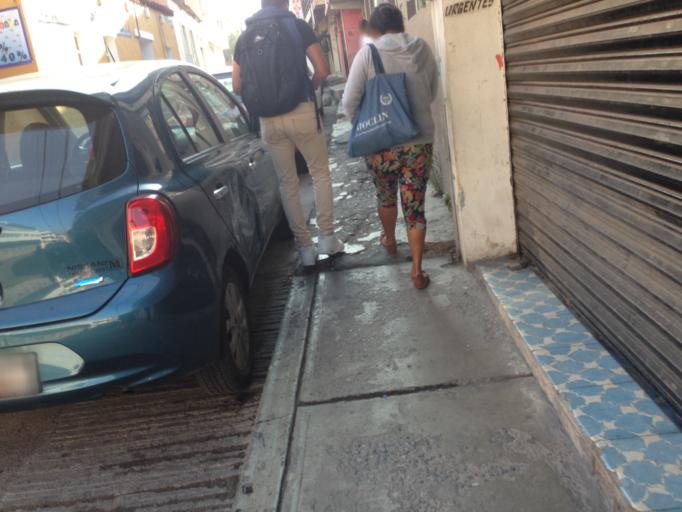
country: MX
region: Guerrero
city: Chilpancingo de los Bravos
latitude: 17.5534
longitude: -99.4994
